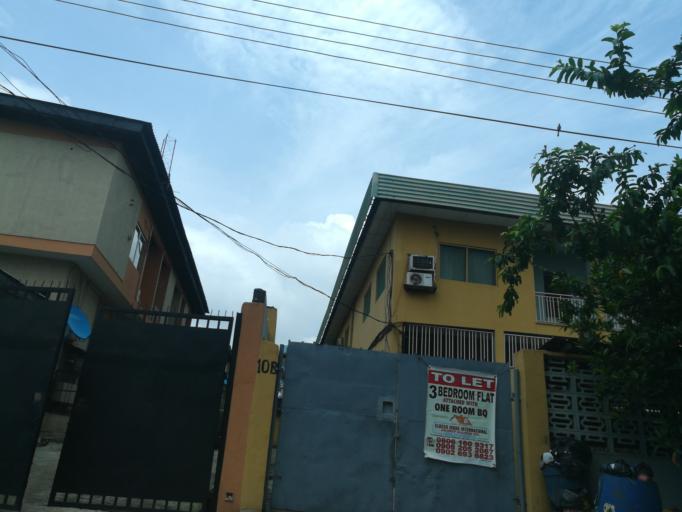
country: NG
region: Lagos
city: Oshodi
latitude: 6.5447
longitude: 3.3323
